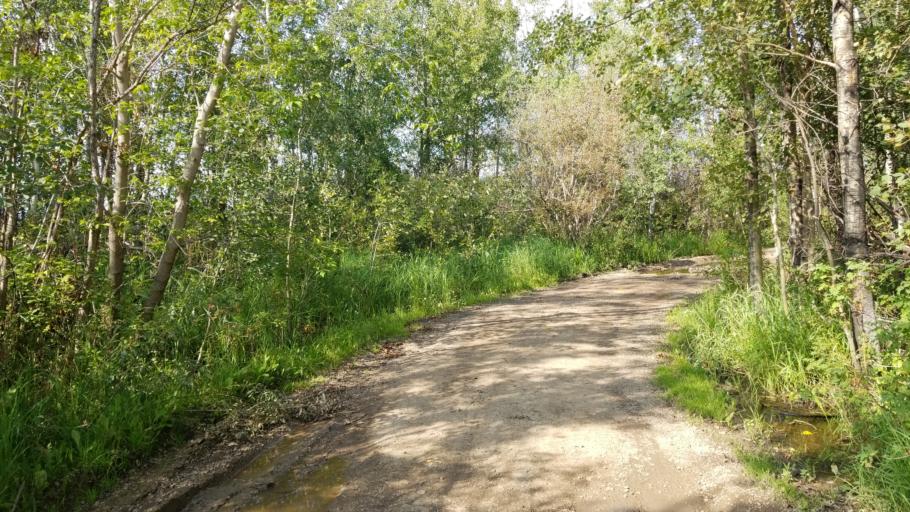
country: CA
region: Saskatchewan
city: Lloydminster
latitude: 53.2587
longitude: -110.0480
